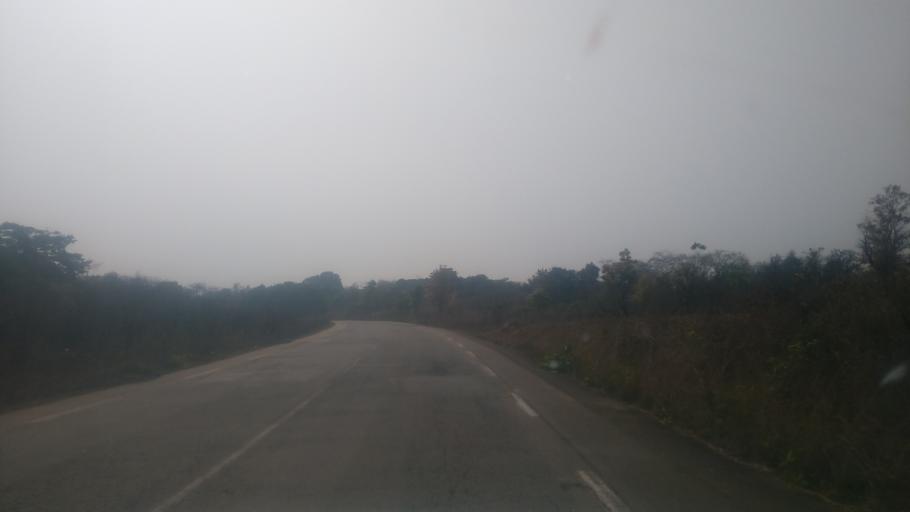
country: CM
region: Centre
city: Ndikinimeki
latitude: 4.8063
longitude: 10.9860
